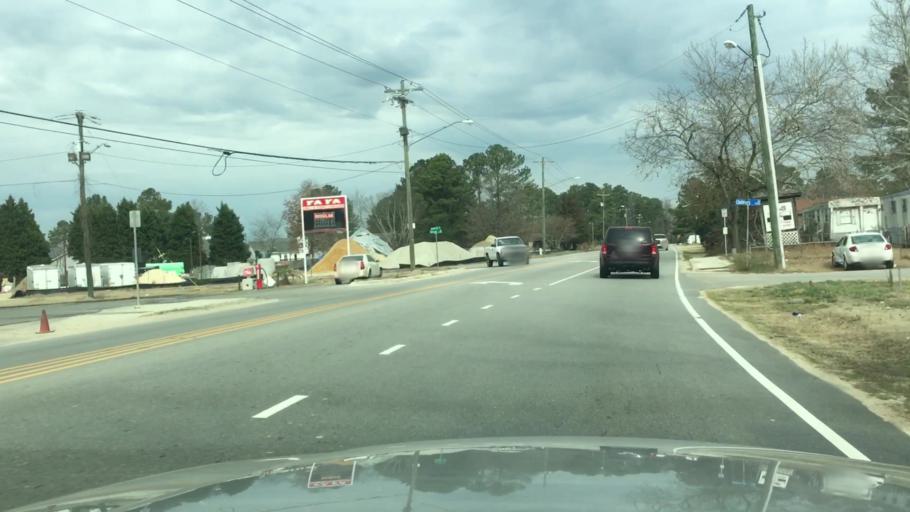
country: US
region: North Carolina
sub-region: Hoke County
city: Rockfish
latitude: 35.0244
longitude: -79.0024
